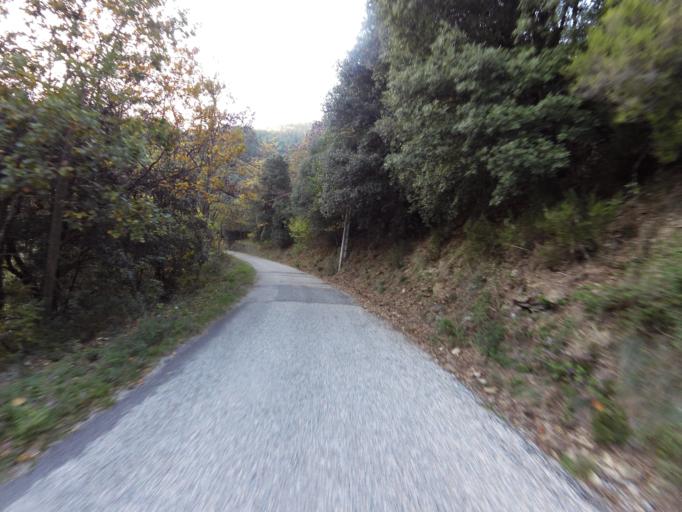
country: FR
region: Rhone-Alpes
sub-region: Departement de l'Ardeche
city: Les Vans
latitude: 44.5283
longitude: 4.1062
